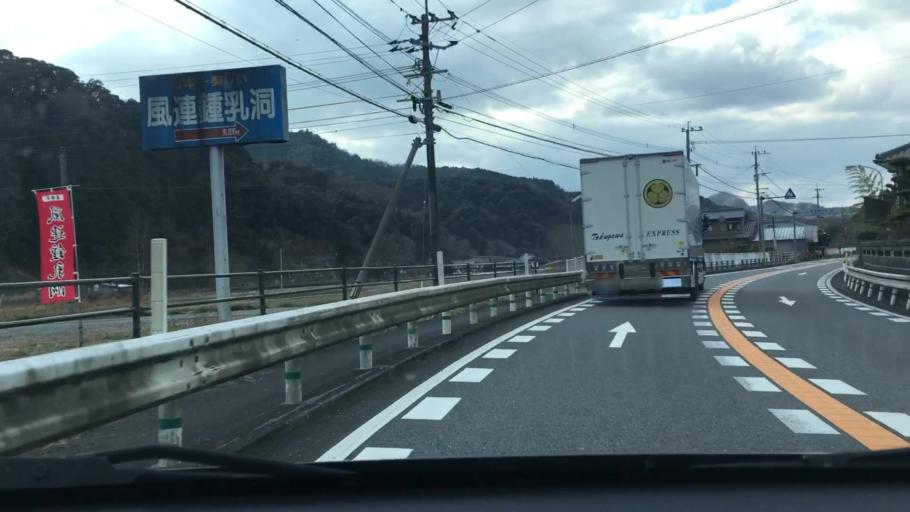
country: JP
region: Oita
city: Usuki
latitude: 33.0051
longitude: 131.7358
